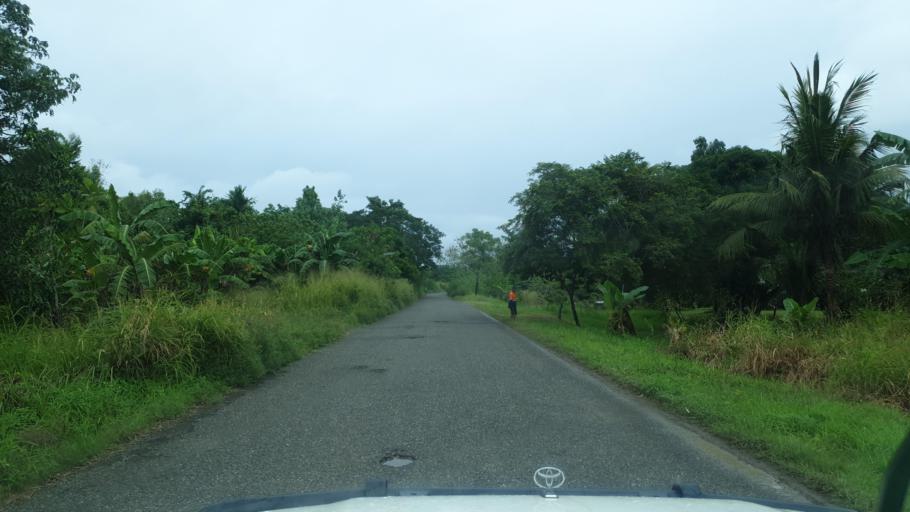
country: PG
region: Gulf
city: Kerema
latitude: -8.3362
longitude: 146.3218
